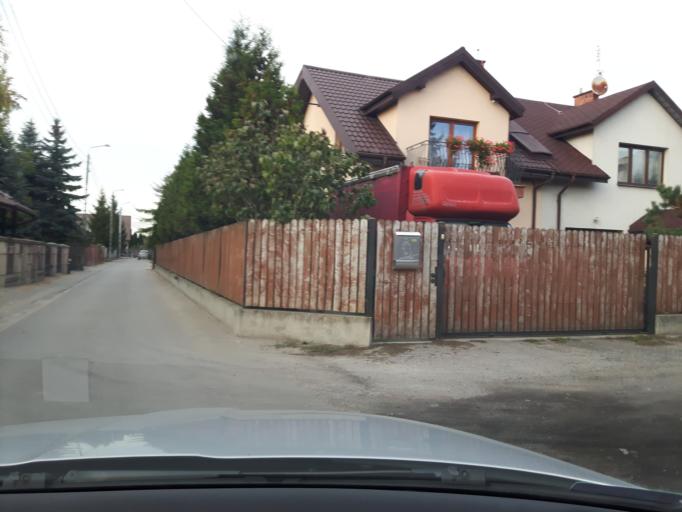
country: PL
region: Masovian Voivodeship
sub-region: Powiat wolominski
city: Zabki
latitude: 52.2831
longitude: 21.1204
